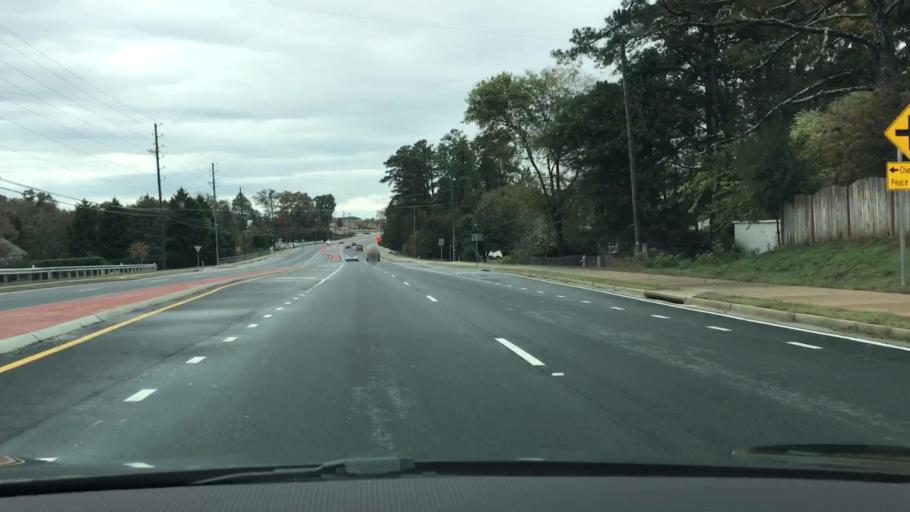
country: US
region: Georgia
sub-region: Fulton County
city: Johns Creek
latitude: 34.1082
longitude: -84.1477
